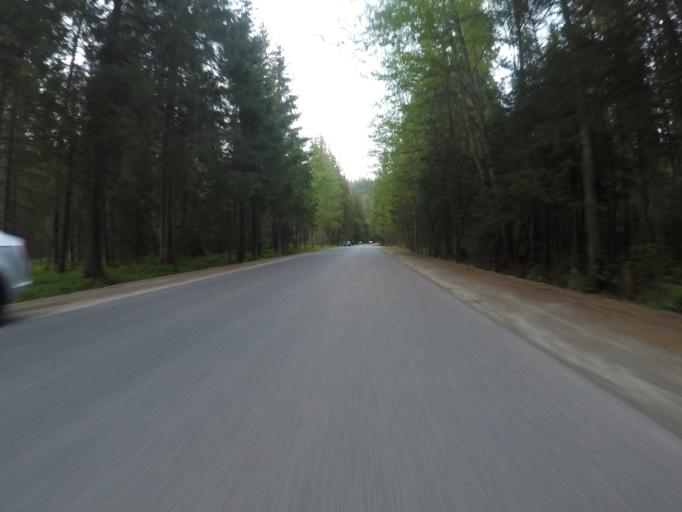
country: PL
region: Lesser Poland Voivodeship
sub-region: Powiat tatrzanski
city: Bukowina Tatrzanska
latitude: 49.2573
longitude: 20.1055
